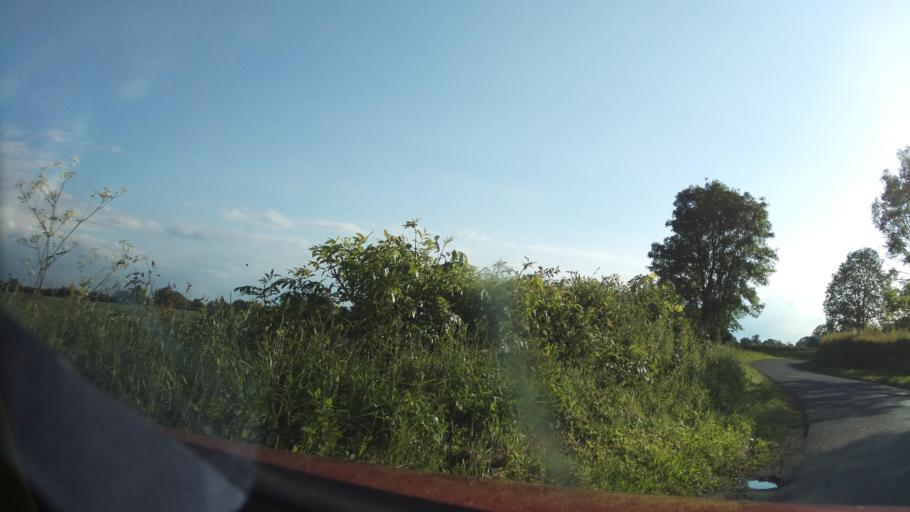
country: GB
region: England
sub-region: Lincolnshire
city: Navenby
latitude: 53.1180
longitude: -0.6366
